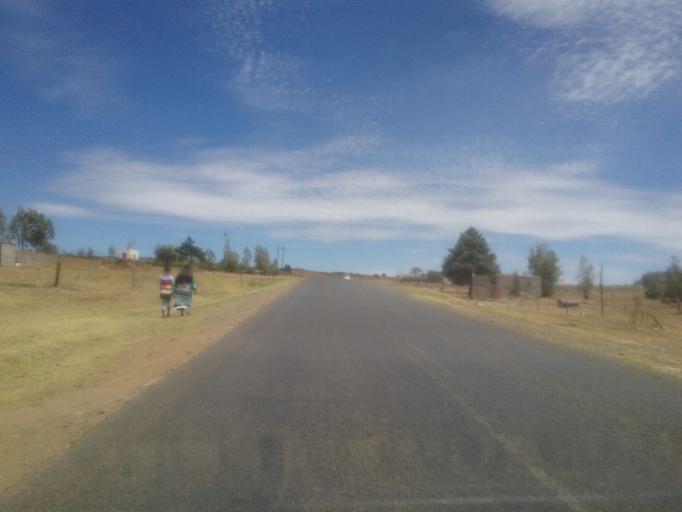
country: LS
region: Mafeteng
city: Mafeteng
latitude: -29.9875
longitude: 27.3290
